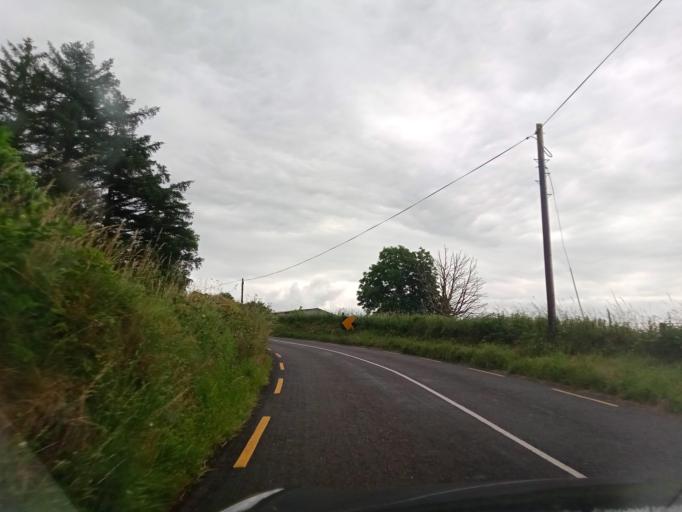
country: IE
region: Leinster
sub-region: Laois
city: Stradbally
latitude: 52.9232
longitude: -7.1935
